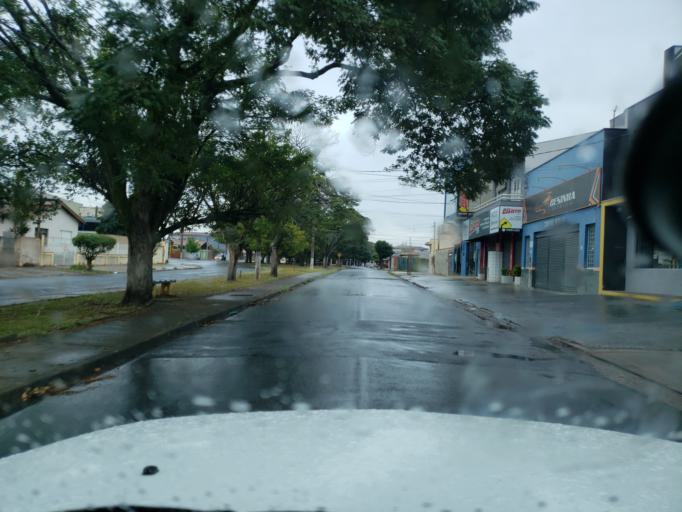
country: BR
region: Sao Paulo
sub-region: Moji-Guacu
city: Mogi-Gaucu
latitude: -22.3547
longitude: -46.9437
